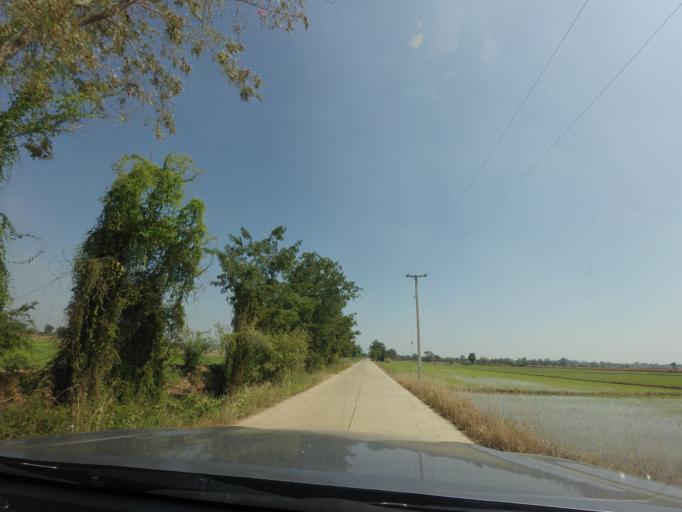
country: TH
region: Sukhothai
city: Sawankhalok
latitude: 17.2747
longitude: 99.8094
